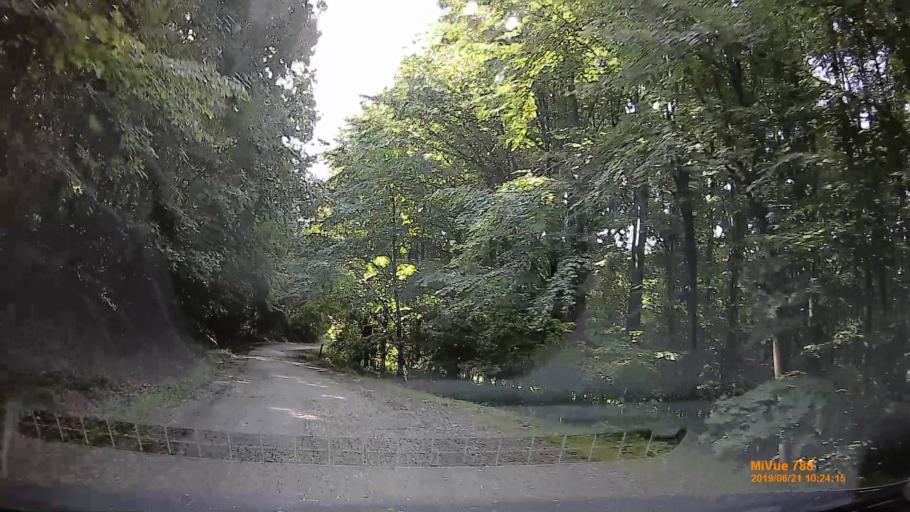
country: HU
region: Baranya
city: Buekkoesd
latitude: 46.1822
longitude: 17.9720
